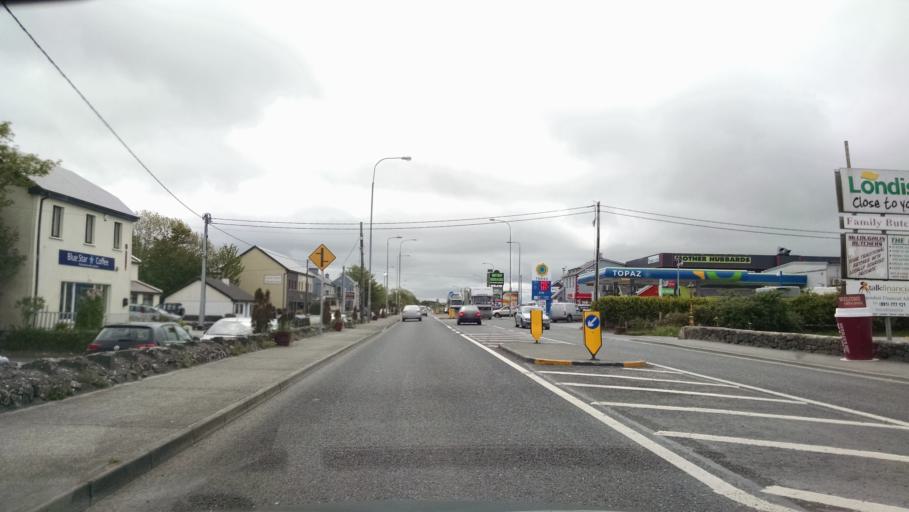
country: IE
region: Connaught
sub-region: County Galway
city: Oranmore
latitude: 53.2095
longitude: -8.8688
